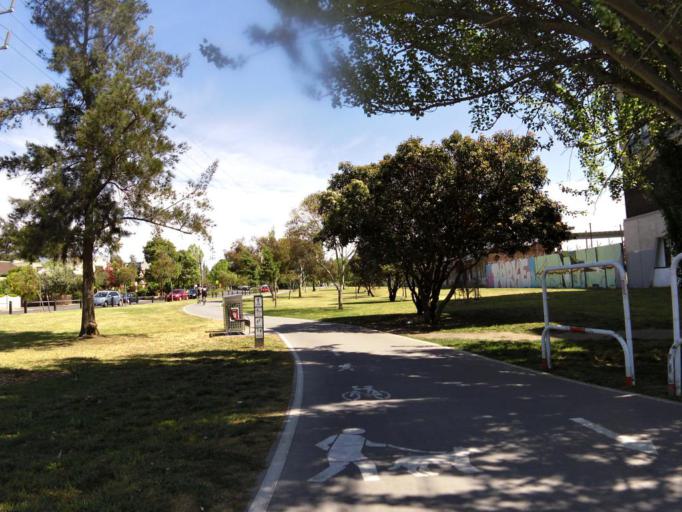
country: AU
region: Victoria
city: Carlton North
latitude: -37.7791
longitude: 144.9705
